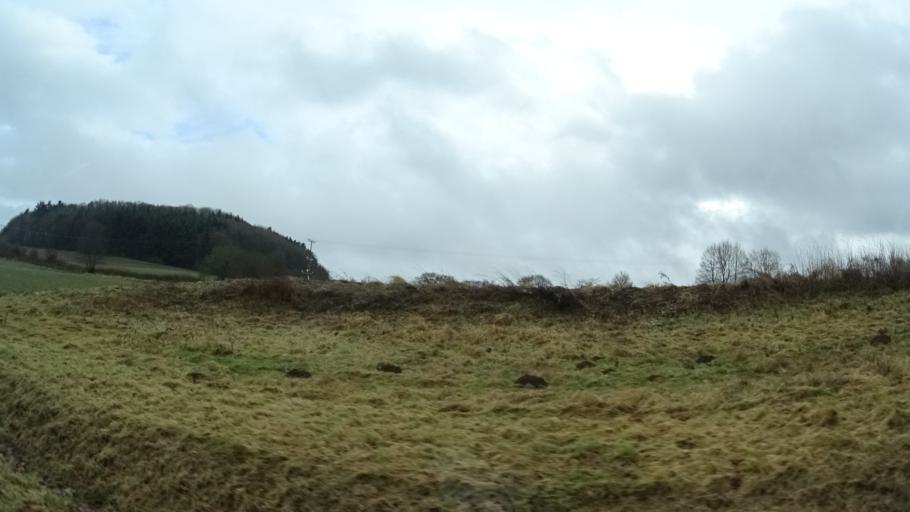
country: DE
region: Hesse
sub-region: Regierungsbezirk Giessen
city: Schotten
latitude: 50.5677
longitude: 9.1063
